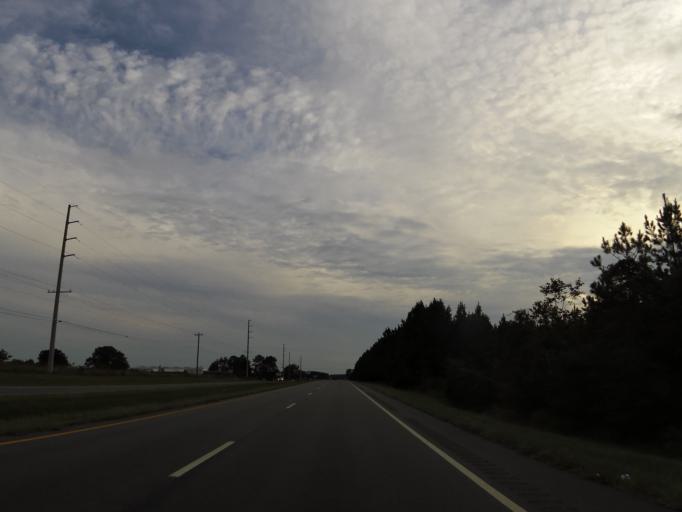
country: US
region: Alabama
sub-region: Escambia County
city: Atmore
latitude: 31.0747
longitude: -87.4847
